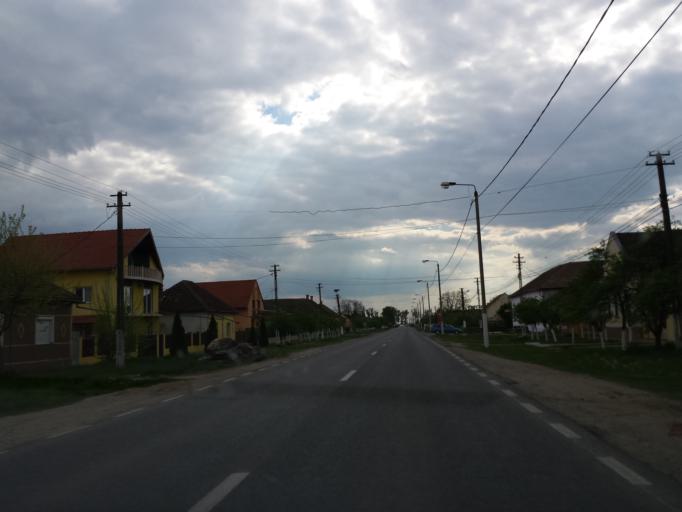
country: RO
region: Timis
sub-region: Comuna Cenad
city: Cenad
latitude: 46.1325
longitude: 20.5735
